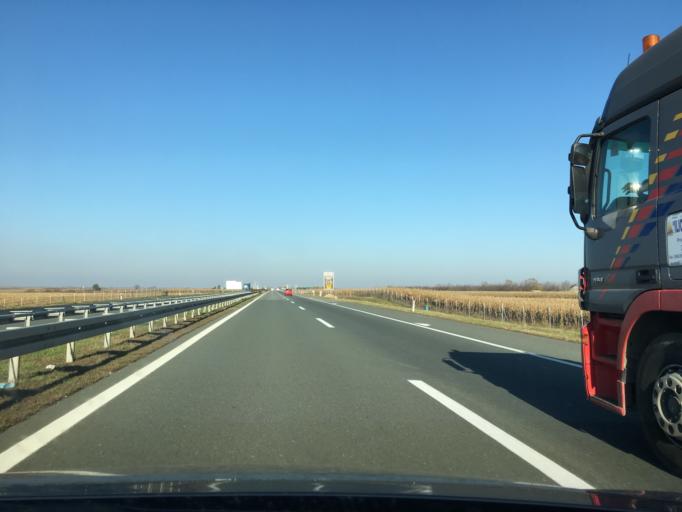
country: RS
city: Rumenka
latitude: 45.3209
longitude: 19.7899
